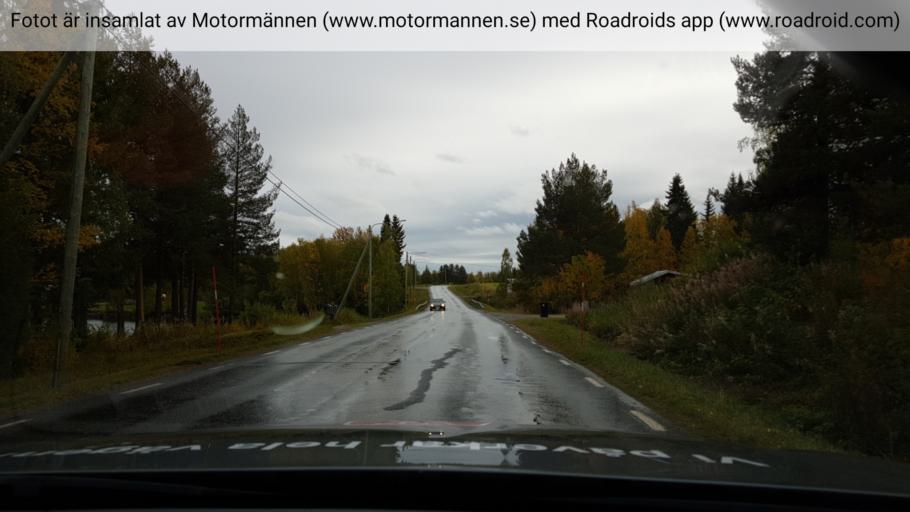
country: SE
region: Vaesterbotten
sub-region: Vilhelmina Kommun
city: Sjoberg
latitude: 64.6426
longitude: 16.3556
